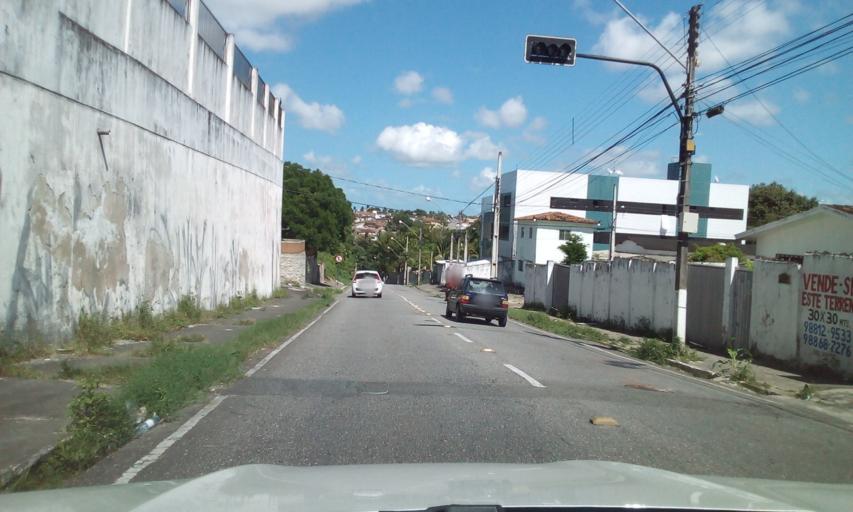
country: BR
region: Paraiba
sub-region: Joao Pessoa
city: Joao Pessoa
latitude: -7.1384
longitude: -34.8797
